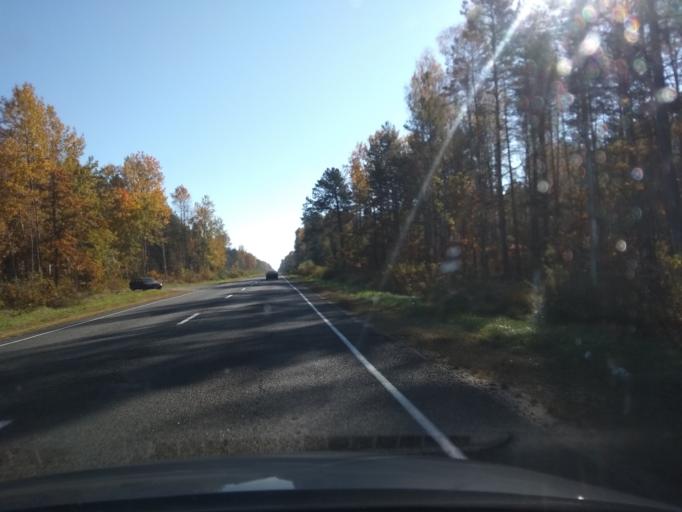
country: BY
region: Brest
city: Malaryta
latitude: 51.9021
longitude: 24.1199
